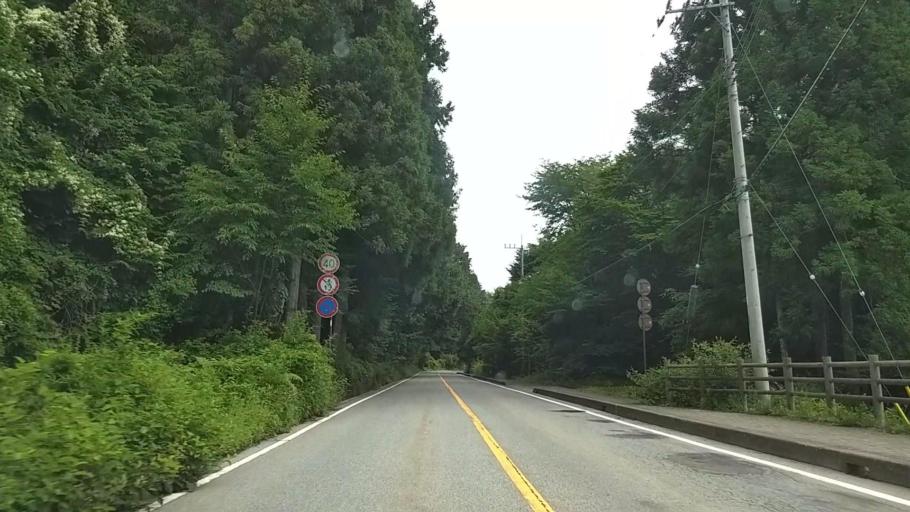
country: JP
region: Yamanashi
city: Fujikawaguchiko
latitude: 35.4991
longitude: 138.6541
